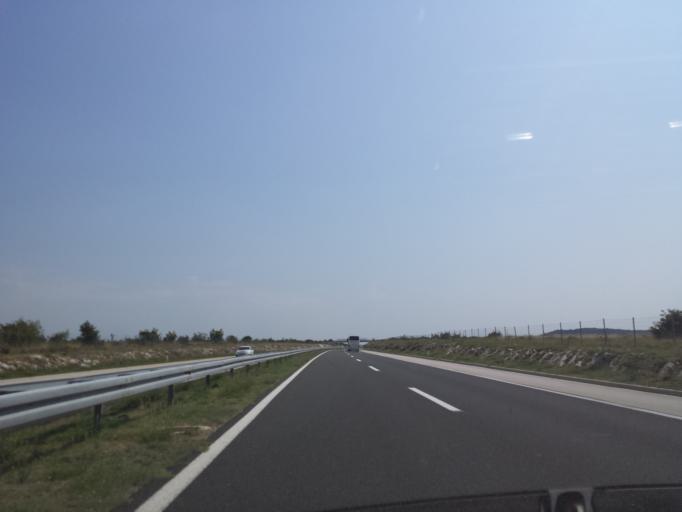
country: HR
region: Zadarska
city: Polaca
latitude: 44.0907
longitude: 15.4914
